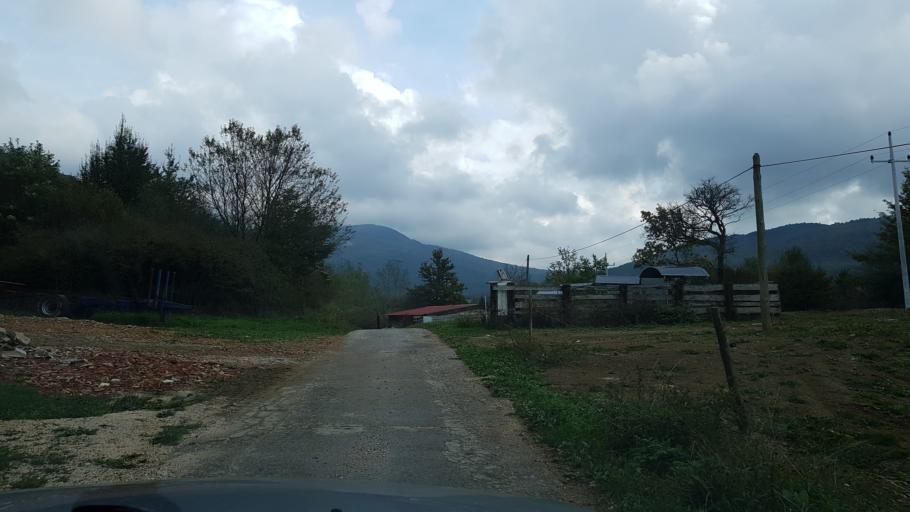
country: HR
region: Istarska
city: Buzet
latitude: 45.4143
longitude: 14.0943
